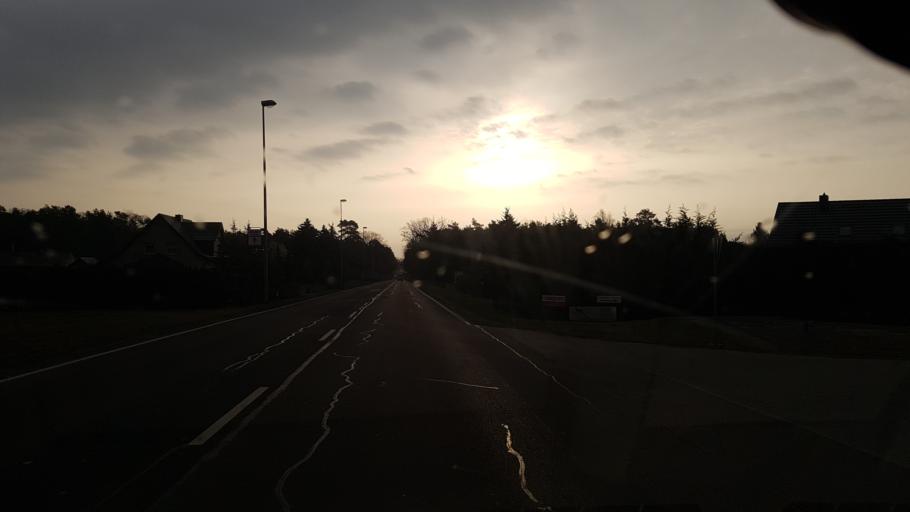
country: DE
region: Brandenburg
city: Kolkwitz
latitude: 51.7536
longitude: 14.1895
